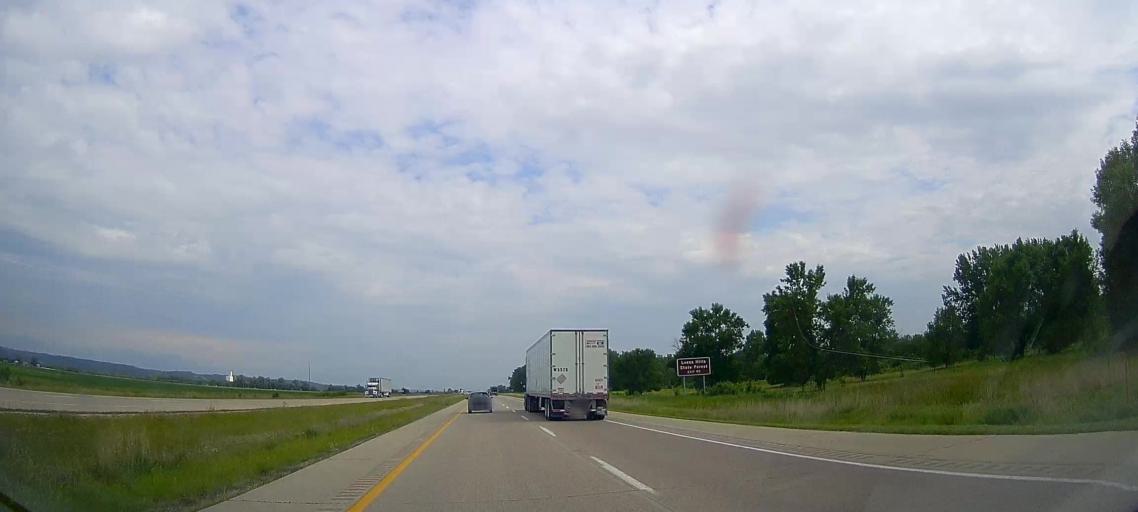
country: US
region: Nebraska
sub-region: Burt County
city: Tekamah
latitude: 41.8142
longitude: -96.0665
